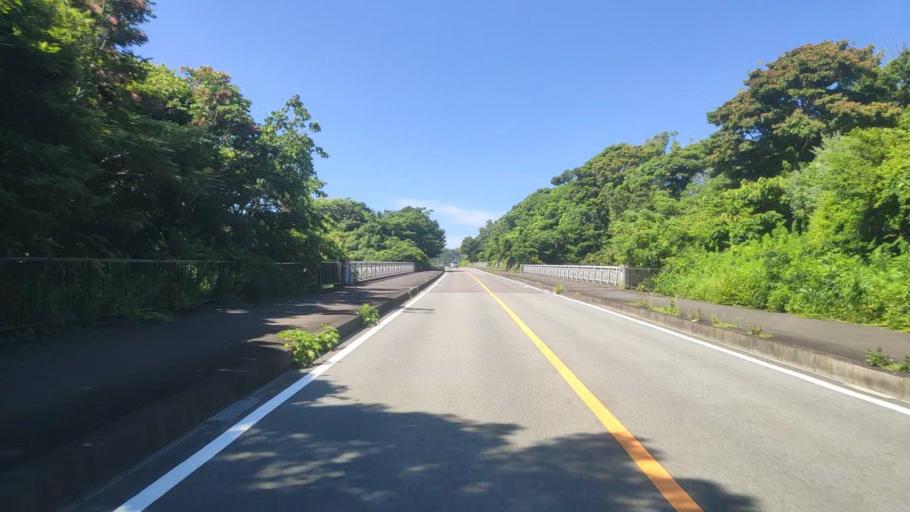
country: JP
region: Wakayama
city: Shingu
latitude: 33.7098
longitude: 135.9968
